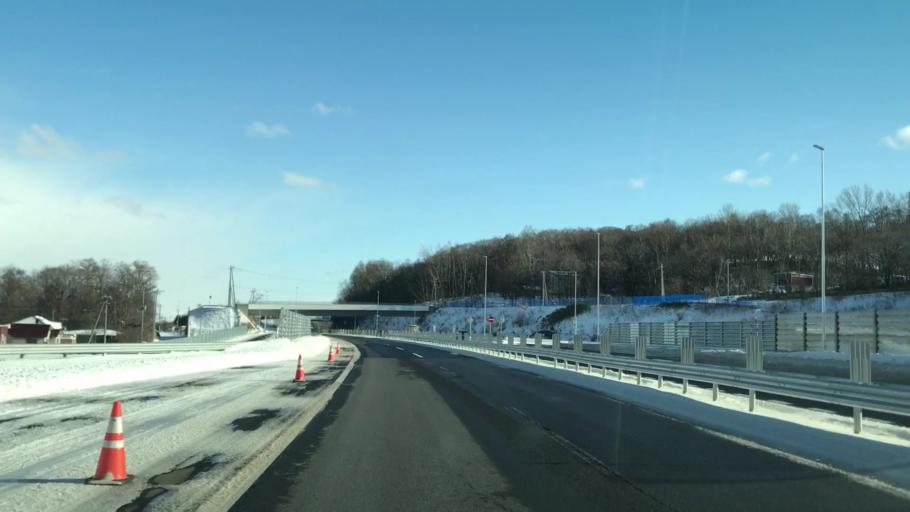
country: JP
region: Hokkaido
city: Otaru
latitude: 43.1333
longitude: 141.1739
